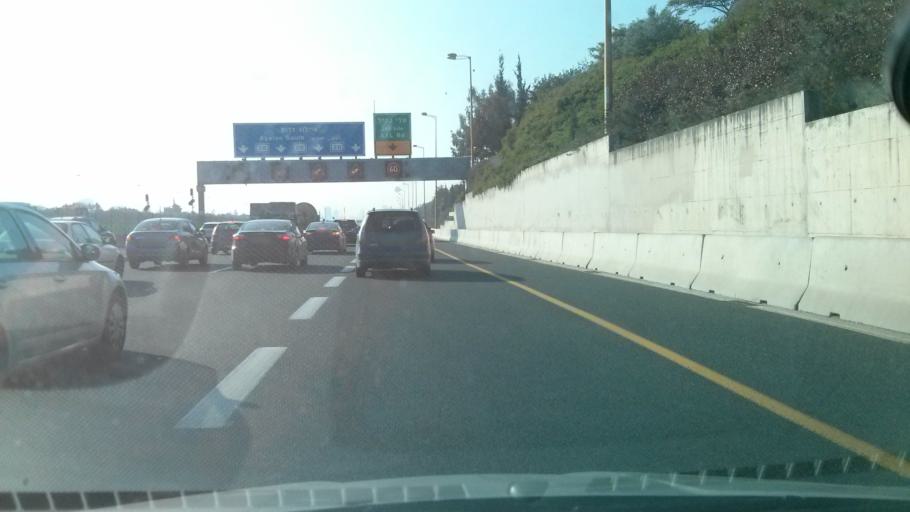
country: IL
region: Tel Aviv
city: Ramat HaSharon
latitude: 32.1270
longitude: 34.8098
